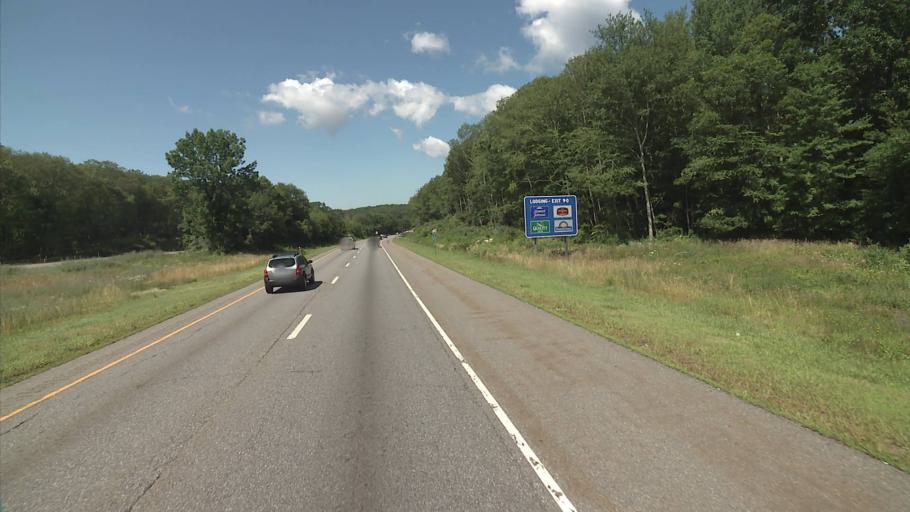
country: US
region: Connecticut
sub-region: New London County
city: Old Mystic
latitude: 41.3732
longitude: -71.9249
